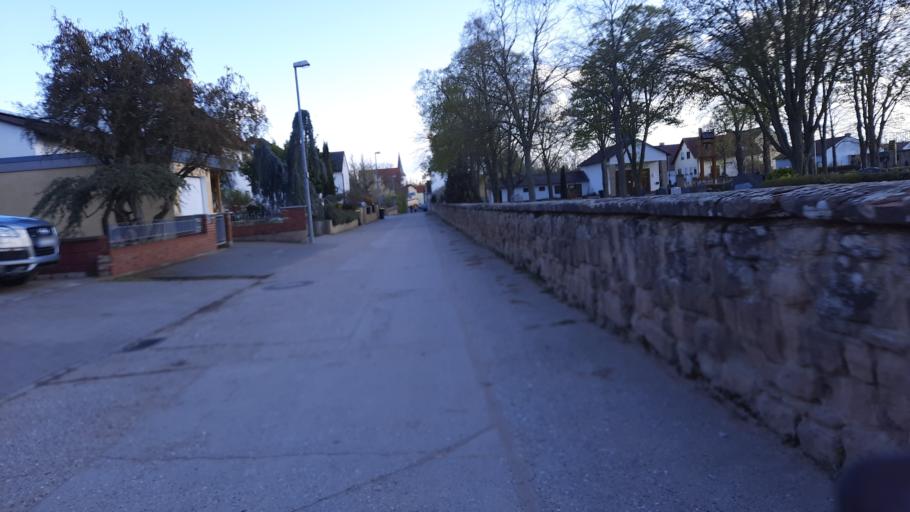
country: DE
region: Rheinland-Pfalz
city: Offstein
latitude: 49.6085
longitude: 8.2627
